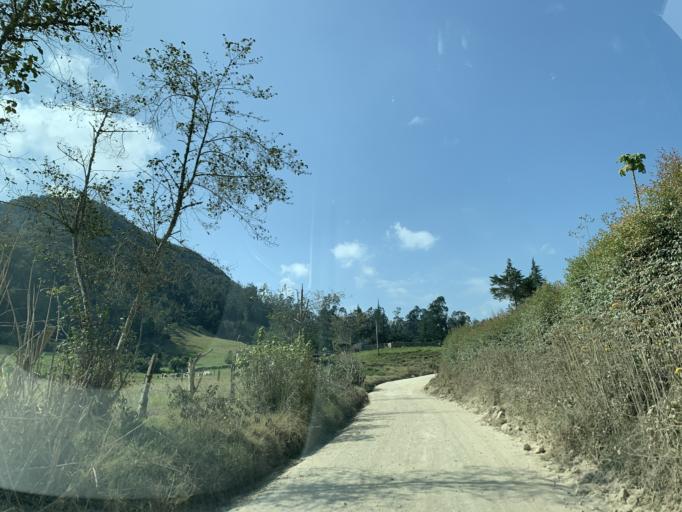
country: CO
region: Boyaca
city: Turmeque
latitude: 5.2963
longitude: -73.5004
